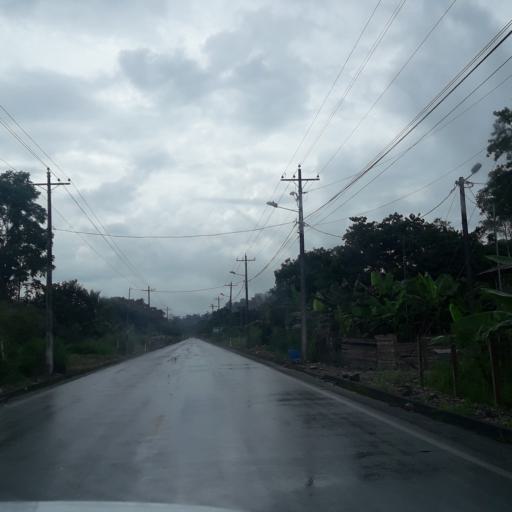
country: EC
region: Napo
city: Tena
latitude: -1.0654
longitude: -77.6455
